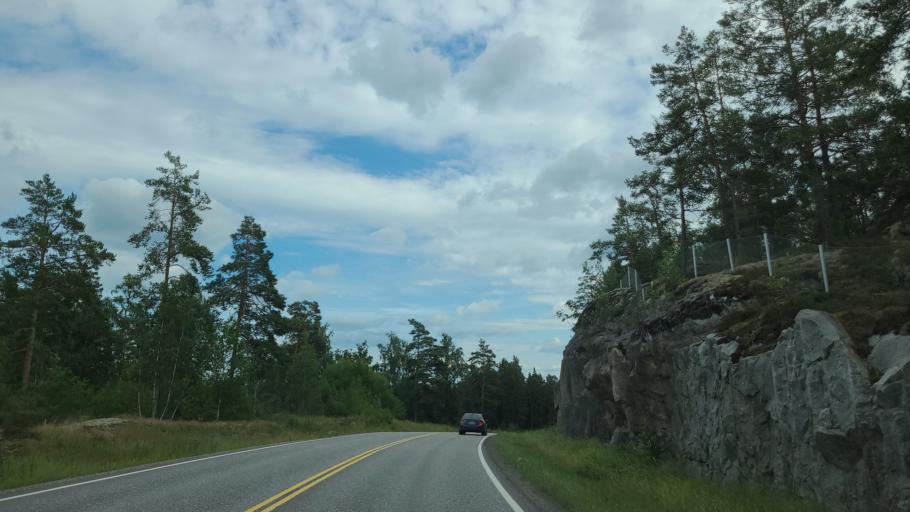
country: FI
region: Varsinais-Suomi
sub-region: Turku
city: Rymaettylae
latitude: 60.3896
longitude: 21.9134
